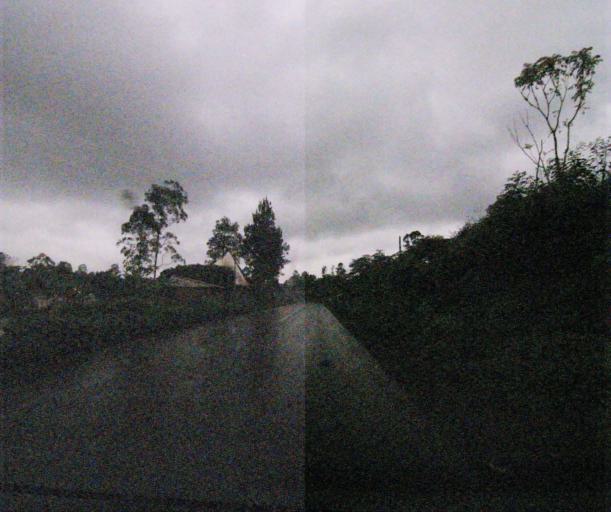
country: CM
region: West
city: Bansoa
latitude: 5.4750
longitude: 10.2858
